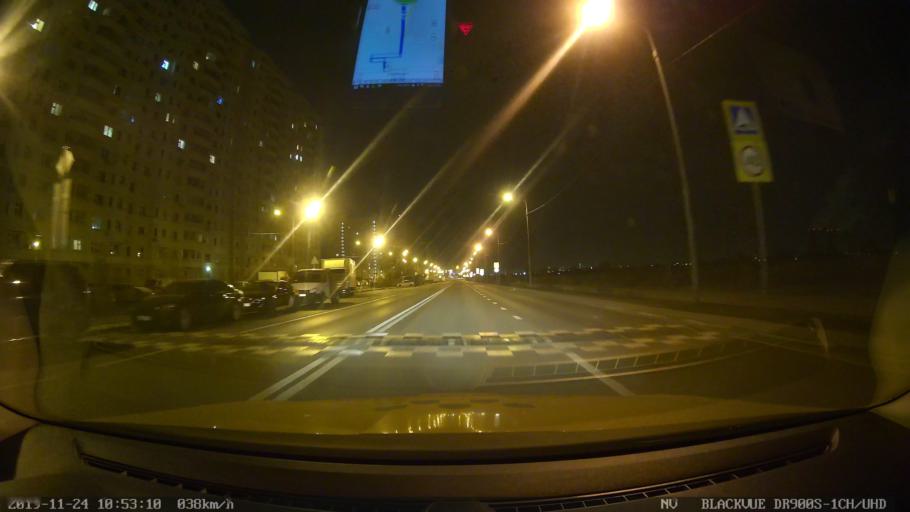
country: RU
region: Moskovskaya
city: Mytishchi
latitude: 55.9125
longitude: 37.7063
